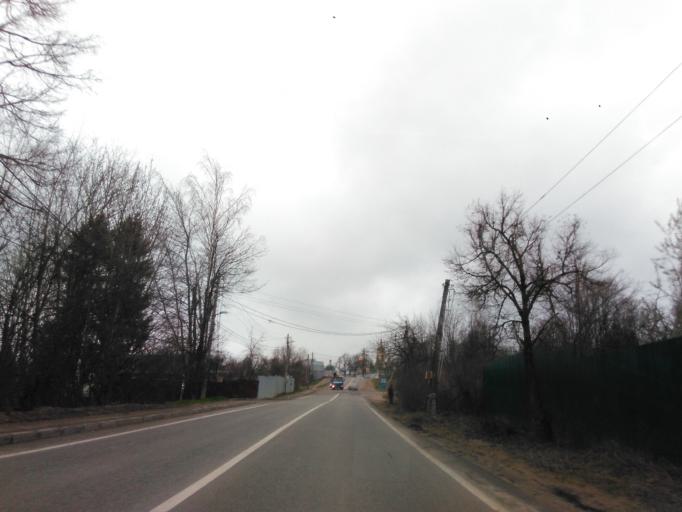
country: RU
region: Moskovskaya
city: Rozhdestveno
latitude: 55.8412
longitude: 37.0048
